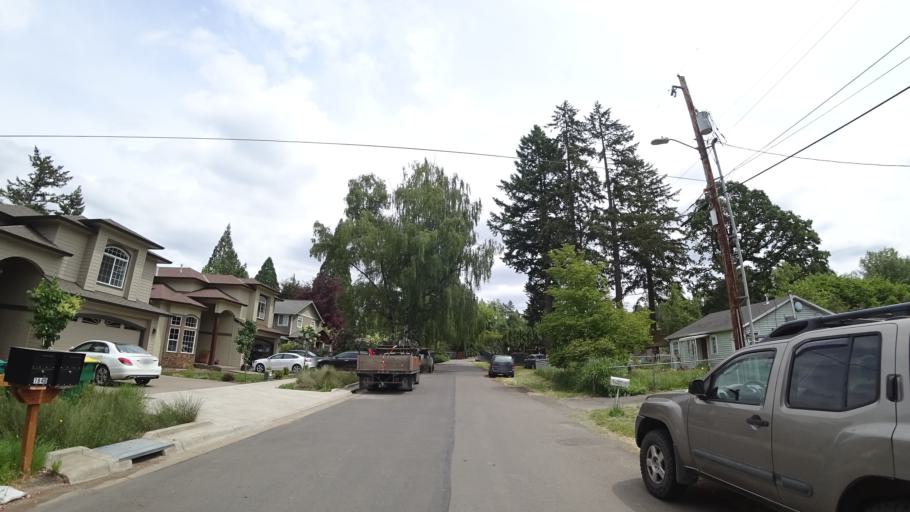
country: US
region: Oregon
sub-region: Washington County
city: Metzger
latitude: 45.4538
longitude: -122.7579
